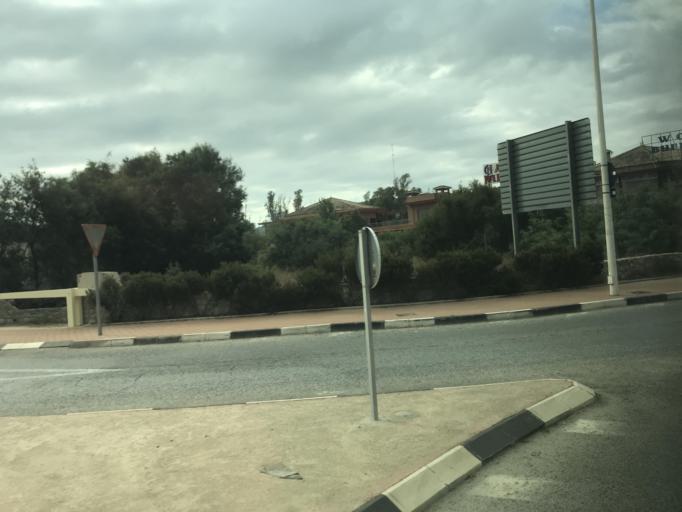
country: ES
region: Valencia
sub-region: Provincia de Alicante
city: Guardamar del Segura
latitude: 38.0953
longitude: -0.6622
